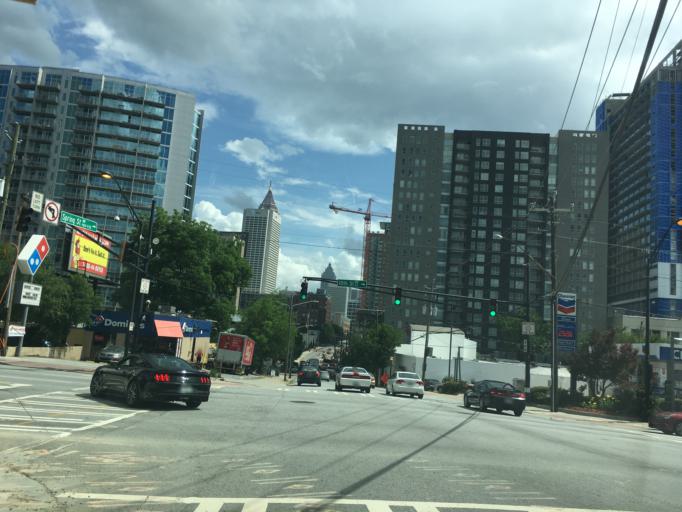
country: US
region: Georgia
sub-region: Fulton County
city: Atlanta
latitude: 33.7817
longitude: -84.3891
